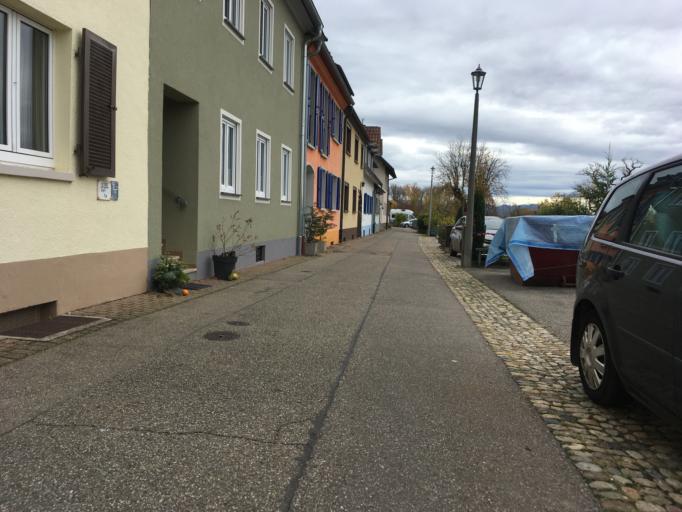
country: DE
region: Baden-Wuerttemberg
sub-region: Freiburg Region
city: Breisach am Rhein
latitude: 48.0303
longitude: 7.5769
